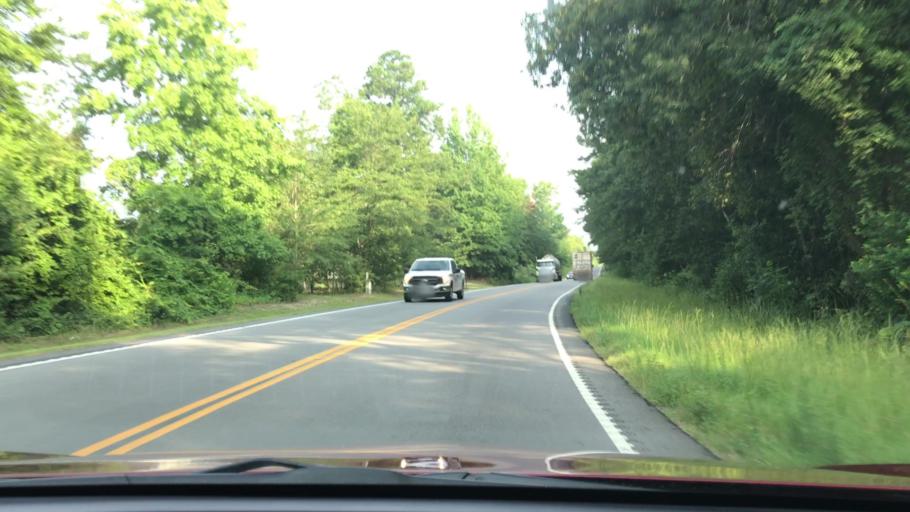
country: US
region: South Carolina
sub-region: Bamberg County
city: Denmark
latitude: 33.5442
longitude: -81.1487
